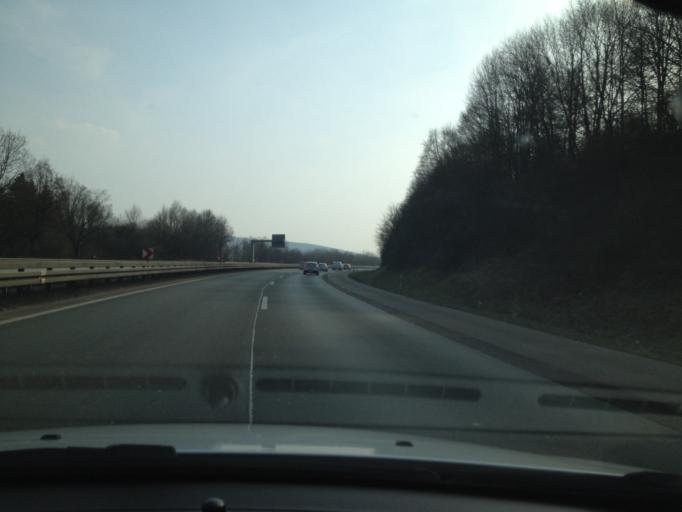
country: DE
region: Hesse
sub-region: Regierungsbezirk Giessen
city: Sinn
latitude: 50.6584
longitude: 8.3193
